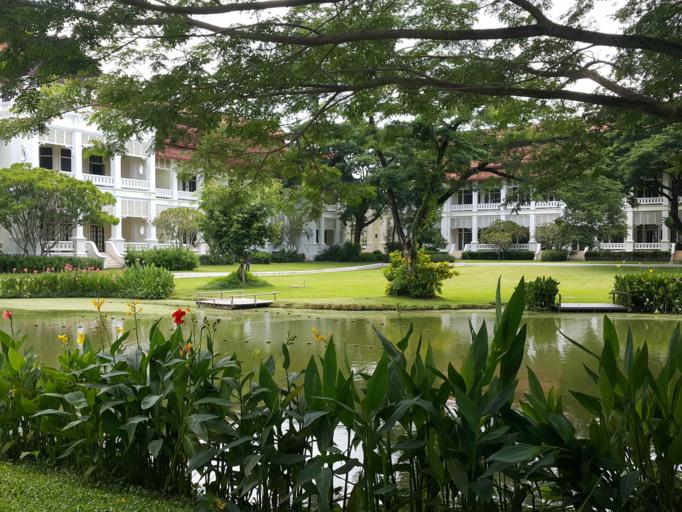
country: TH
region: Chiang Mai
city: Chiang Mai
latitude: 18.7782
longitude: 99.0364
